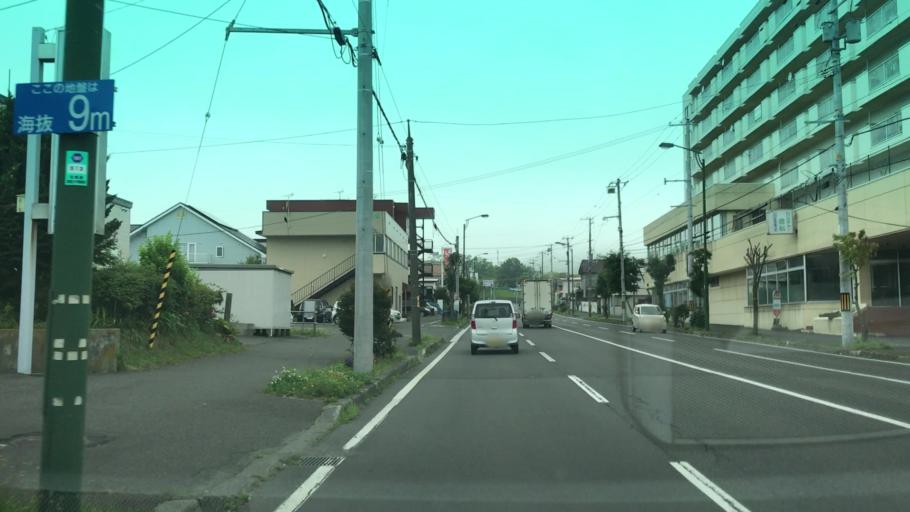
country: JP
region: Hokkaido
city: Muroran
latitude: 42.3634
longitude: 141.0386
